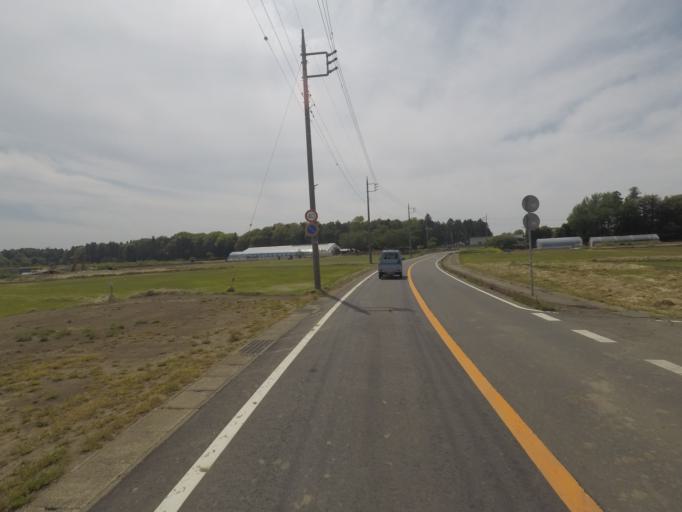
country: JP
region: Ibaraki
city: Ishige
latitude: 36.0950
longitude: 140.0269
